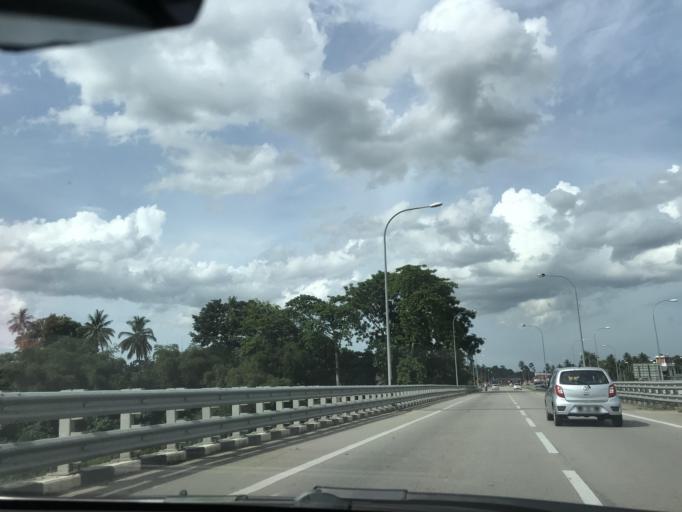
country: MY
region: Kelantan
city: Kampung Lemal
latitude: 6.0321
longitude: 102.1468
